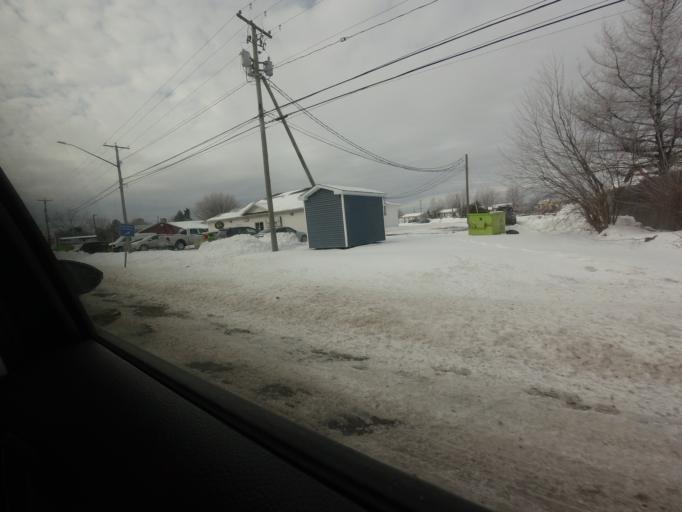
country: CA
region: New Brunswick
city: Oromocto
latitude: 45.8532
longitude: -66.4627
